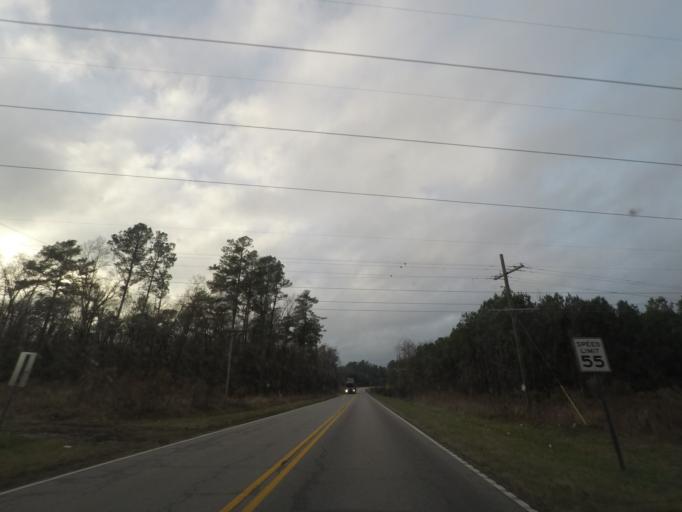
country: US
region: South Carolina
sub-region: Dorchester County
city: Saint George
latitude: 33.0585
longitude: -80.6239
